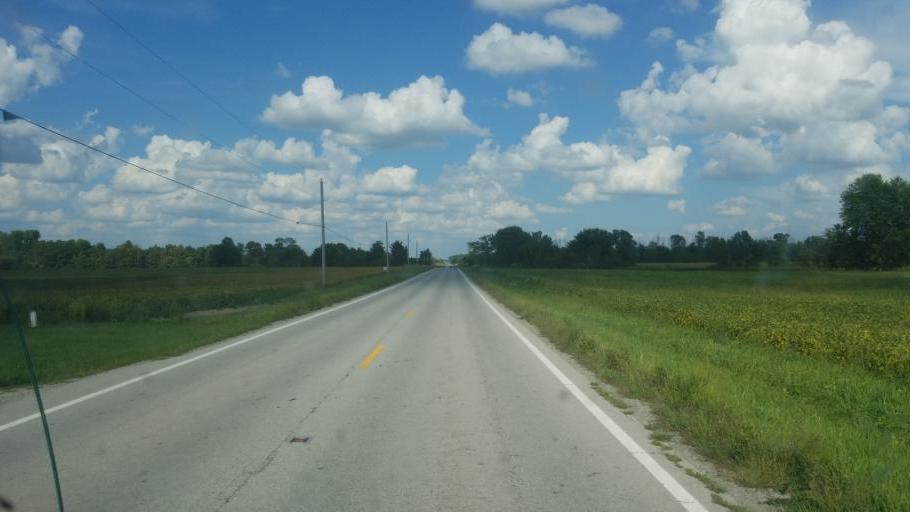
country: US
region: Ohio
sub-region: Seneca County
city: Tiffin
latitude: 40.9809
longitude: -83.1480
